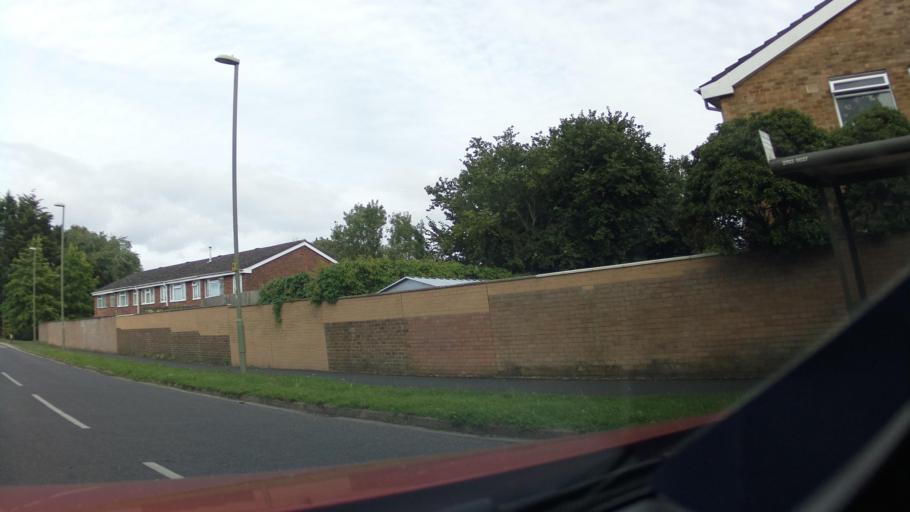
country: GB
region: England
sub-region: Hampshire
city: Eastleigh
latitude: 50.9830
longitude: -1.3692
